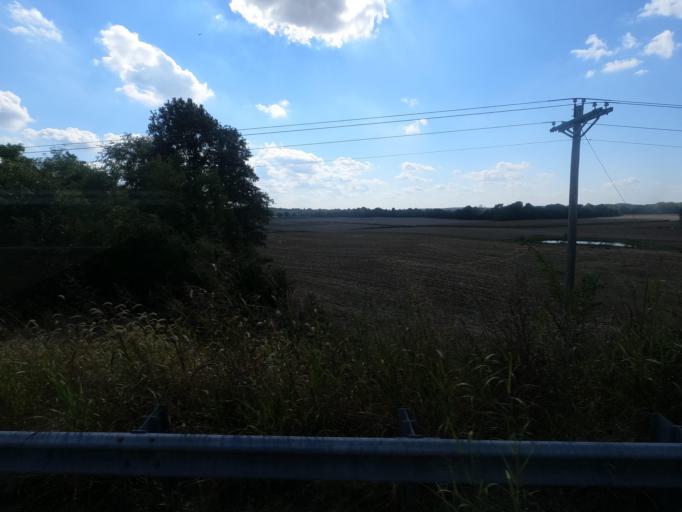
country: US
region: Illinois
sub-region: Massac County
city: Metropolis
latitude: 37.2489
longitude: -88.7398
